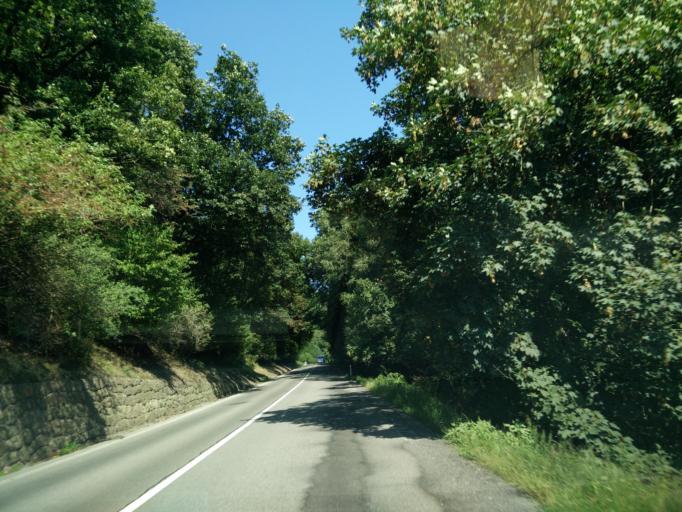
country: SK
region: Banskobystricky
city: Nova Bana
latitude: 48.3998
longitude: 18.6184
